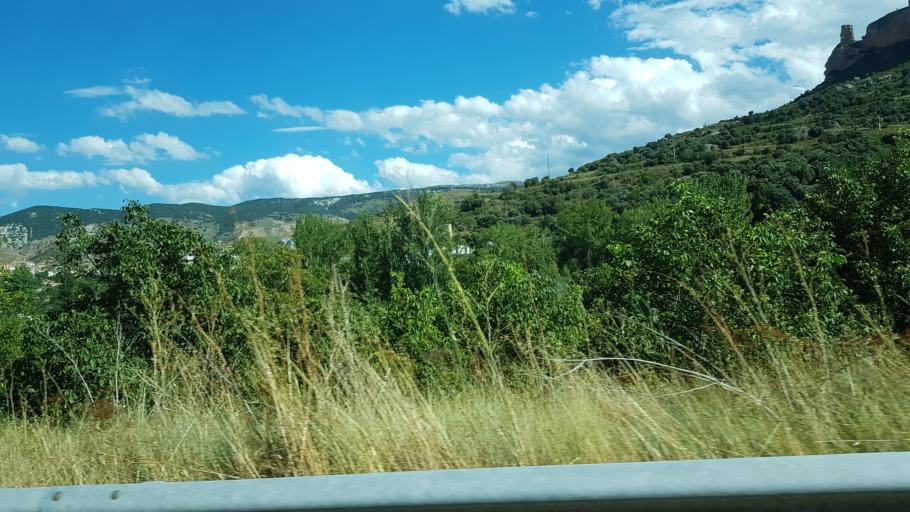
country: ES
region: La Rioja
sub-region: Provincia de La Rioja
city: Viguera
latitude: 42.3105
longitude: -2.5536
